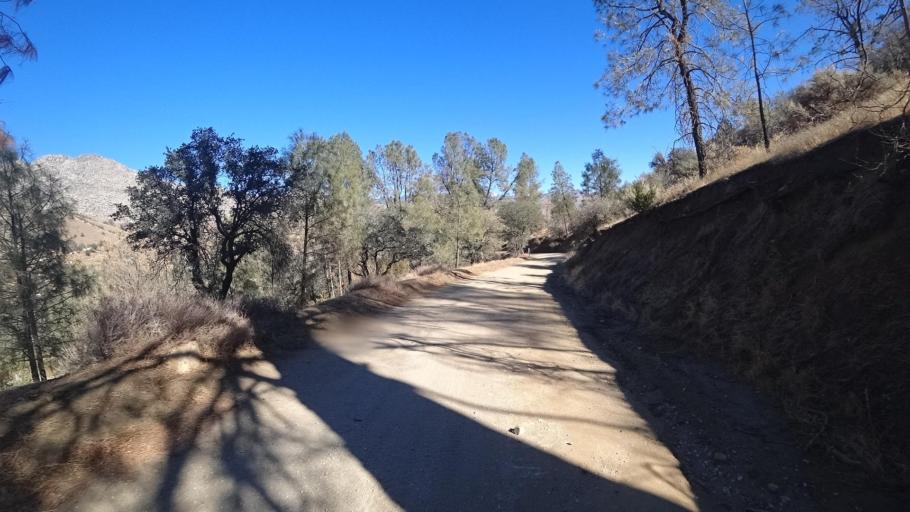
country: US
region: California
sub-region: Kern County
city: Wofford Heights
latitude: 35.7057
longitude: -118.4753
